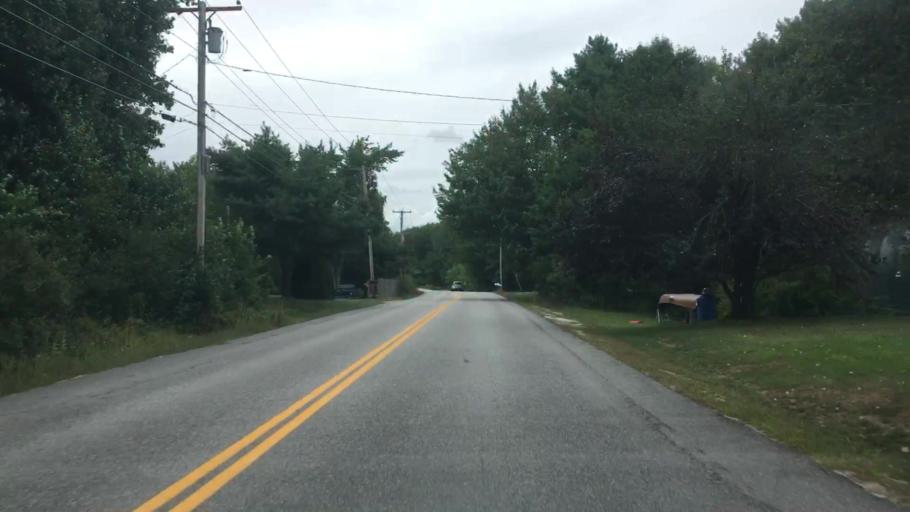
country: US
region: Maine
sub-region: Cumberland County
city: Yarmouth
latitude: 43.8353
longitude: -70.2035
